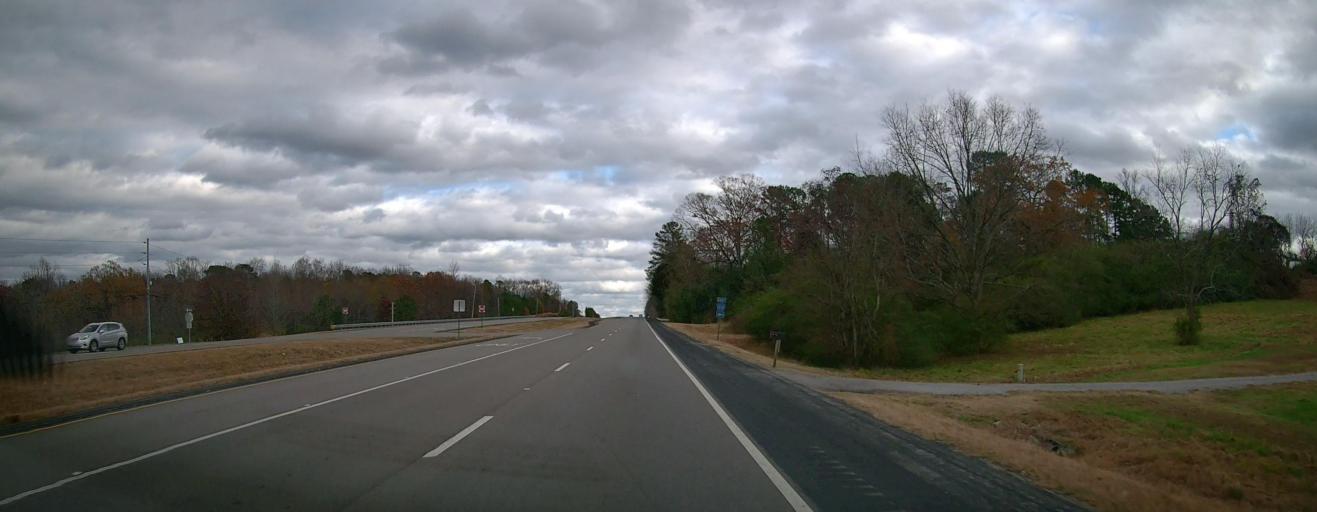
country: US
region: Alabama
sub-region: Cullman County
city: Cullman
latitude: 34.2391
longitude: -86.9474
